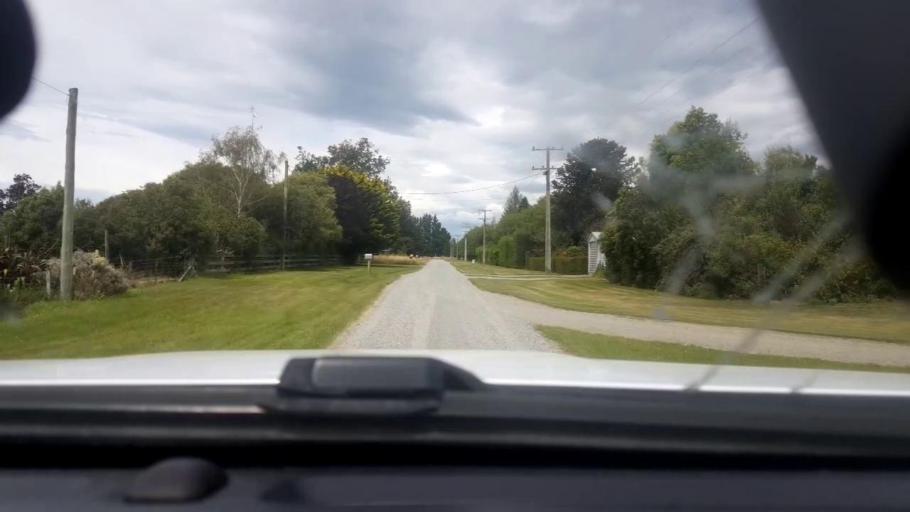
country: NZ
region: Canterbury
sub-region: Timaru District
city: Pleasant Point
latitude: -44.1421
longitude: 171.2896
